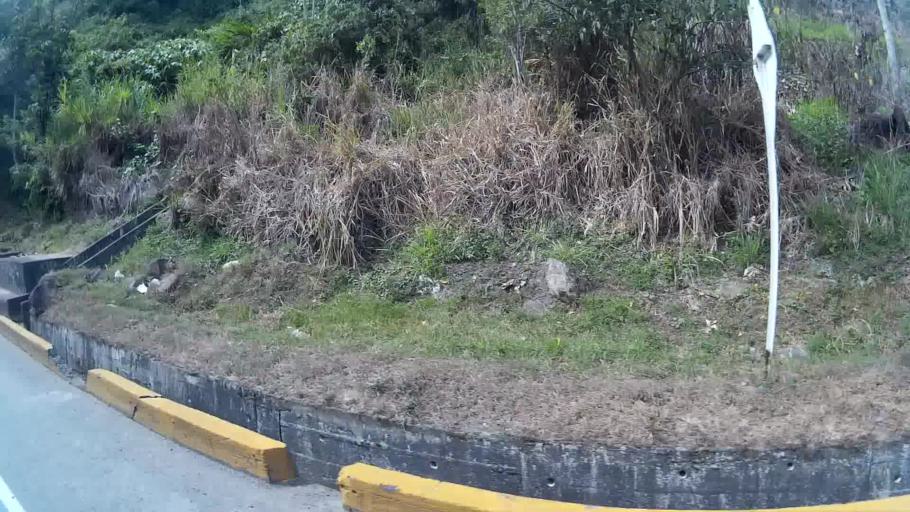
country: CO
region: Risaralda
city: Pereira
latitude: 4.8142
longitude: -75.7444
